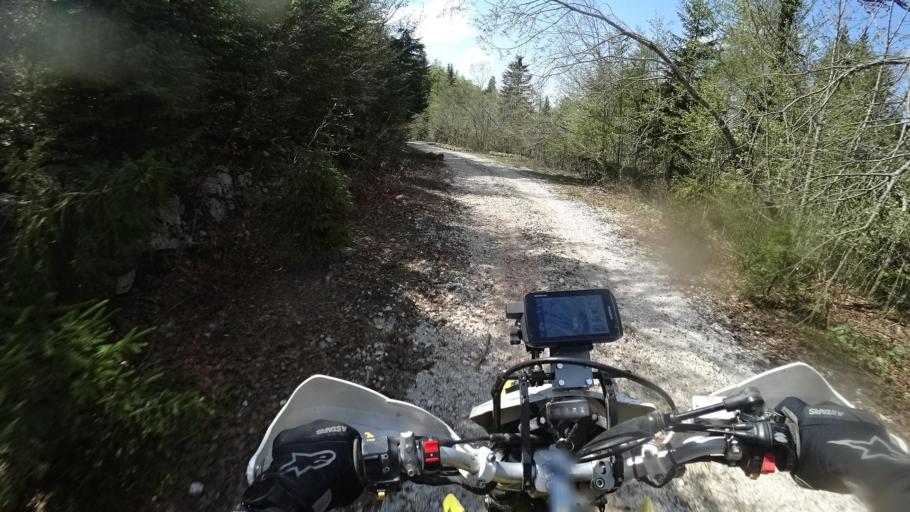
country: BA
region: Republika Srpska
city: Sipovo
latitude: 44.1291
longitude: 17.0349
